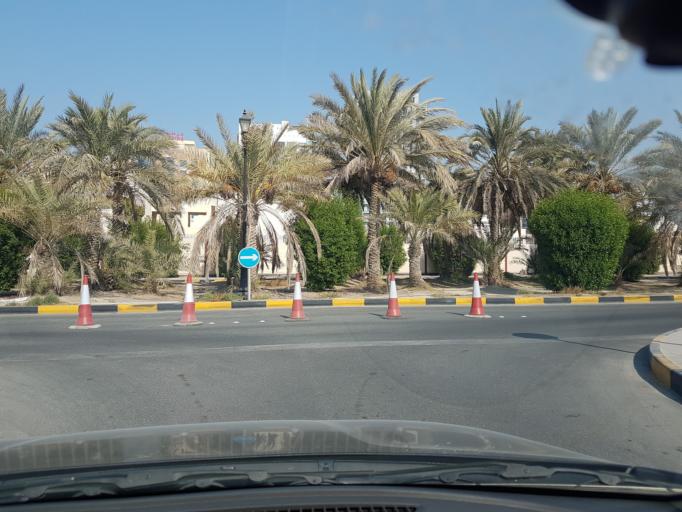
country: BH
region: Manama
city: Manama
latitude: 26.2182
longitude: 50.5992
